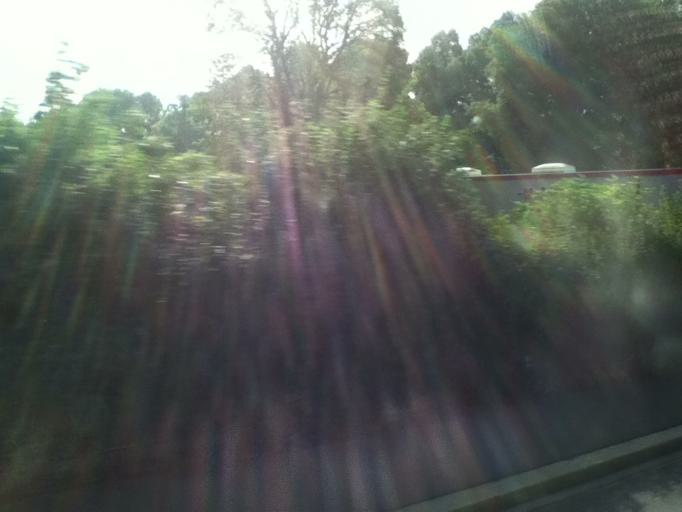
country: DE
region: Saxony
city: Wittgensdorf
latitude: 50.8733
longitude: 12.9080
